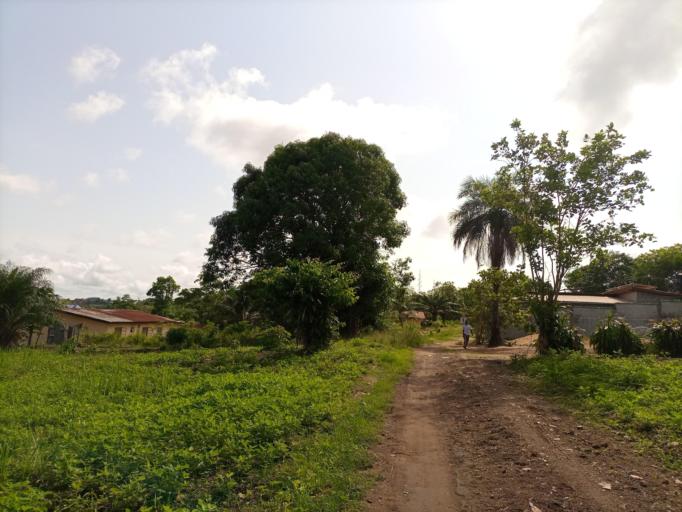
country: SL
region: Southern Province
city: Bo
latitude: 7.9659
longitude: -11.7656
